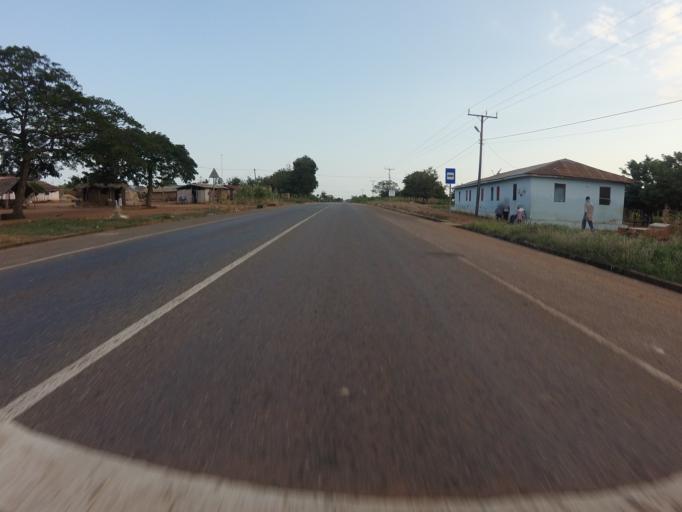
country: GH
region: Volta
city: Anloga
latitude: 6.0734
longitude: 0.6044
